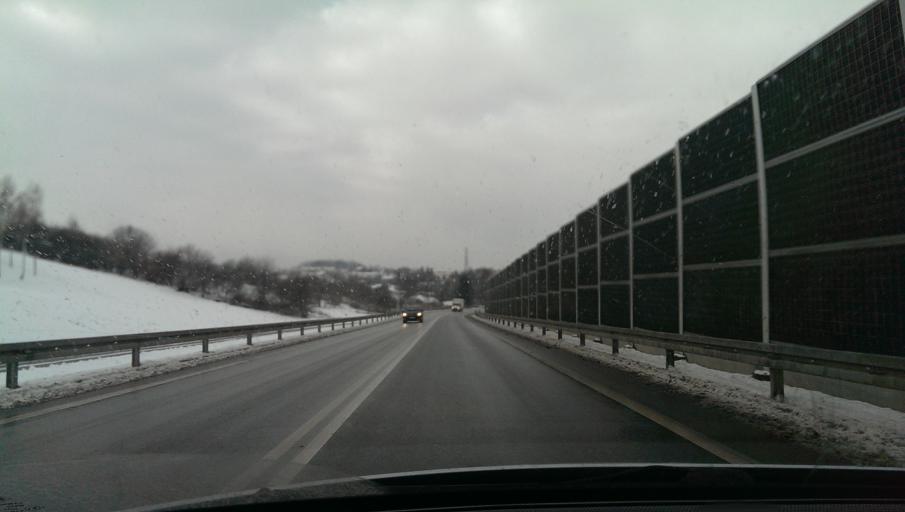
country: PL
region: Subcarpathian Voivodeship
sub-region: Powiat brzozowski
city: Brzozow
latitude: 49.6892
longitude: 22.0343
